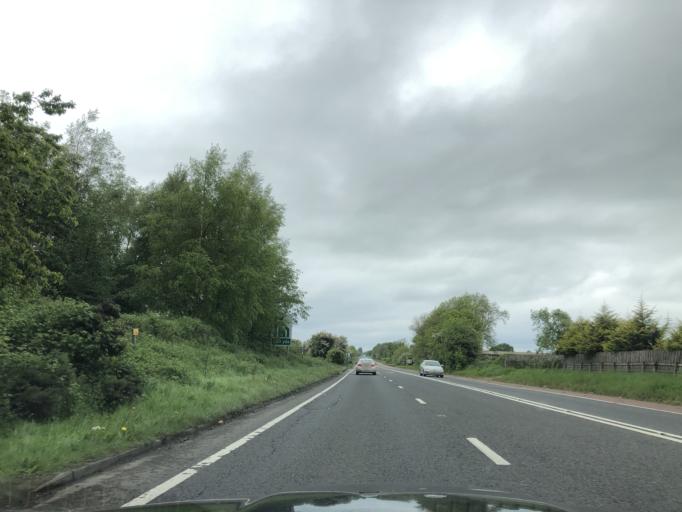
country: GB
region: Northern Ireland
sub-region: Antrim Borough
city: Crumlin
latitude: 54.6366
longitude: -6.1494
